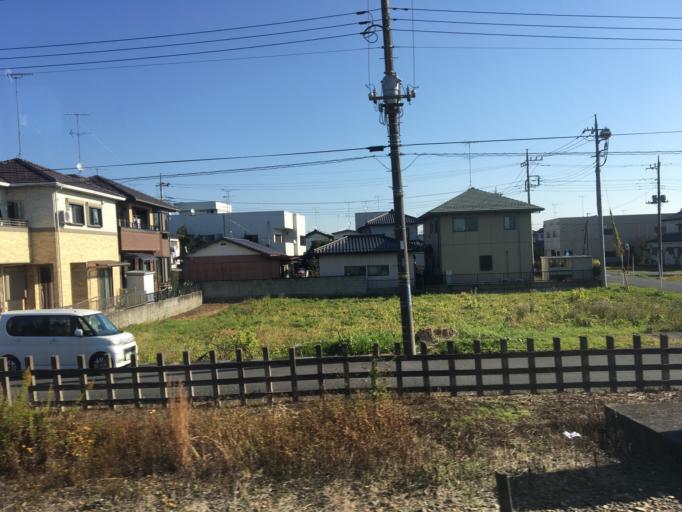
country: JP
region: Saitama
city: Hanyu
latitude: 36.1791
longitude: 139.5315
